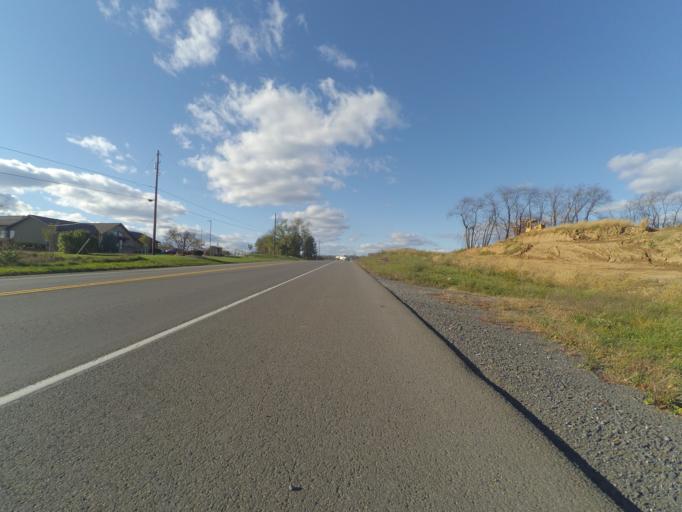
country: US
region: Pennsylvania
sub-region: Centre County
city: Houserville
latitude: 40.8431
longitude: -77.8085
